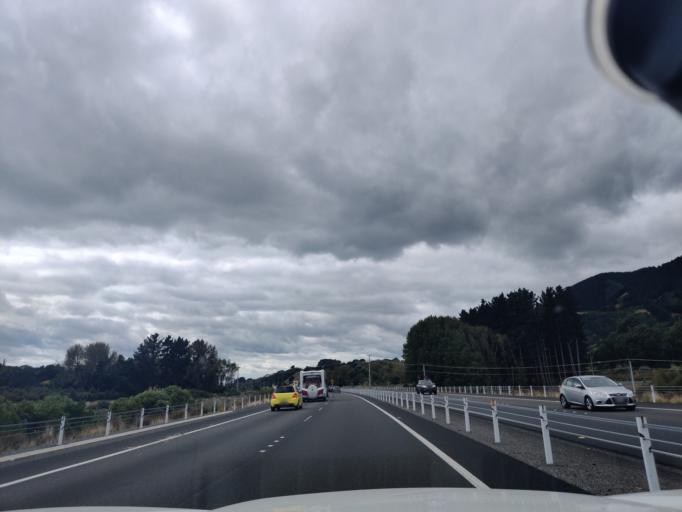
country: NZ
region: Wellington
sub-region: Kapiti Coast District
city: Paraparaumu
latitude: -40.8447
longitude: 175.0823
